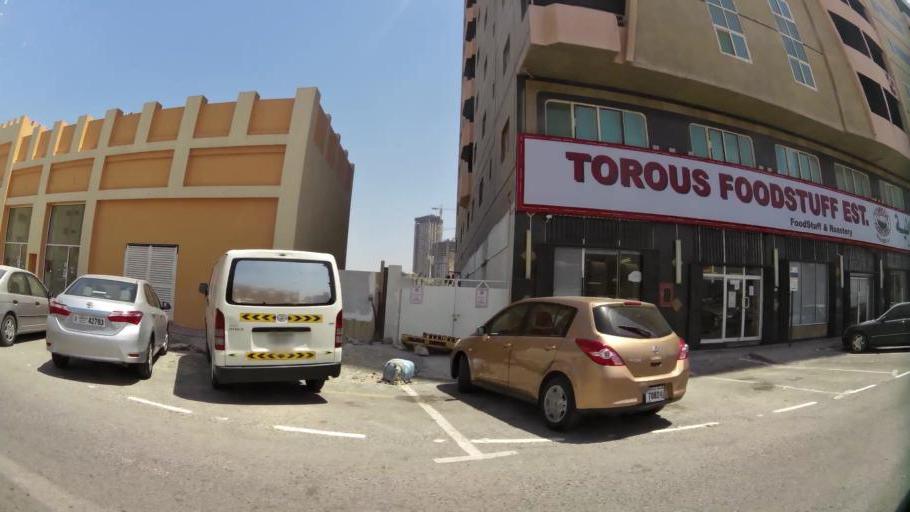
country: AE
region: Ajman
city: Ajman
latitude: 25.3910
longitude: 55.4532
